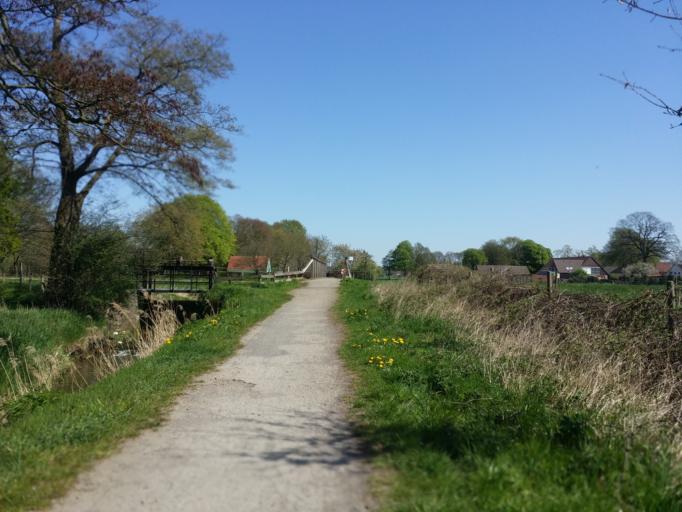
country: DE
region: Lower Saxony
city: Stuhr
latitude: 53.0229
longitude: 8.7065
